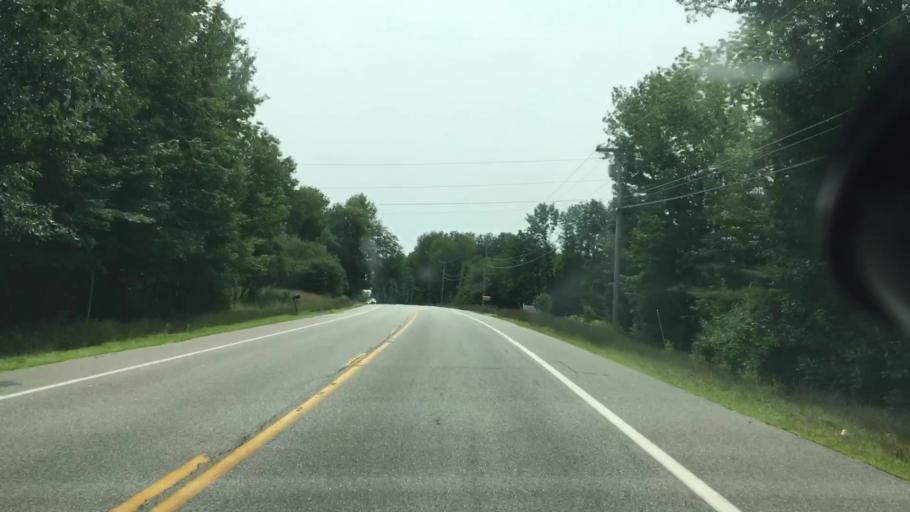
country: US
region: Maine
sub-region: Androscoggin County
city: Livermore Falls
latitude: 44.4298
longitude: -70.1464
